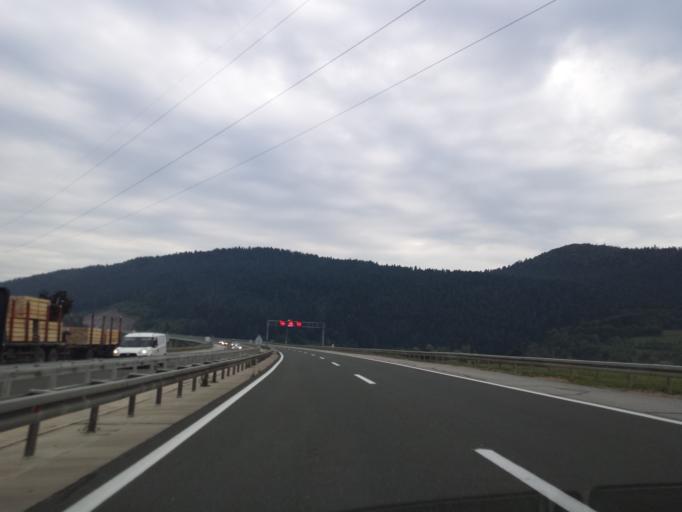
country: HR
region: Licko-Senjska
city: Otocac
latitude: 44.8667
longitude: 15.2079
